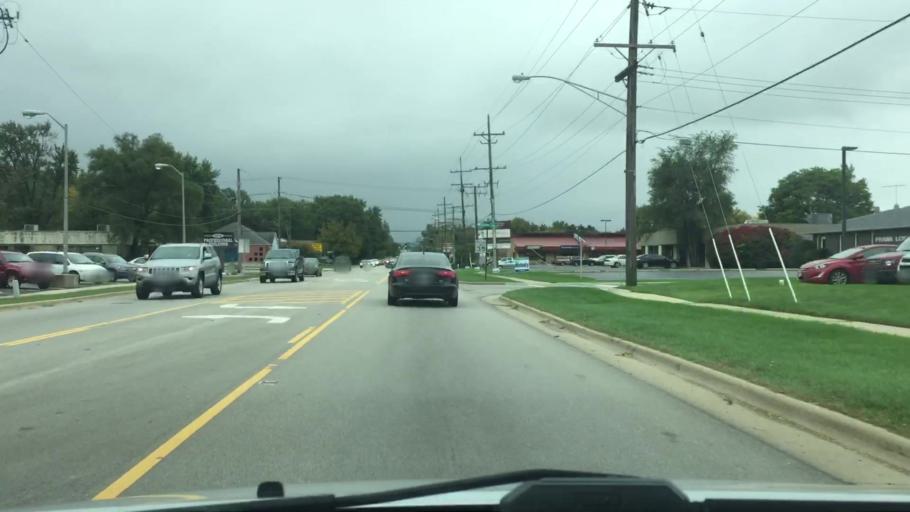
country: US
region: Illinois
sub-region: McHenry County
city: McHenry
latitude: 42.3391
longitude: -88.2747
